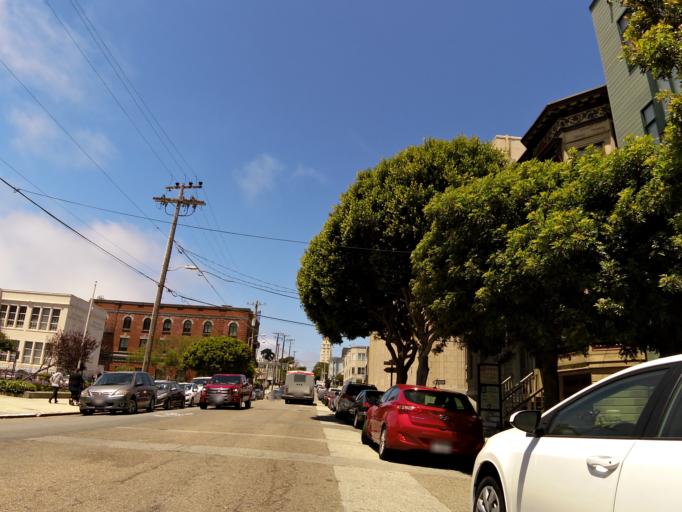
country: US
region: California
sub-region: San Francisco County
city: San Francisco
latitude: 37.7869
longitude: -122.4351
